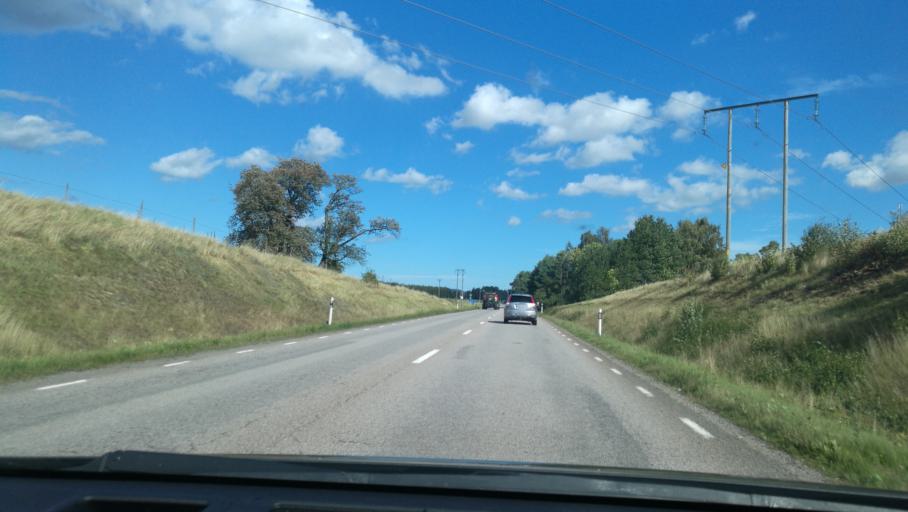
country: SE
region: Vaestra Goetaland
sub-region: Gotene Kommun
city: Kallby
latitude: 58.4951
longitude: 13.2968
